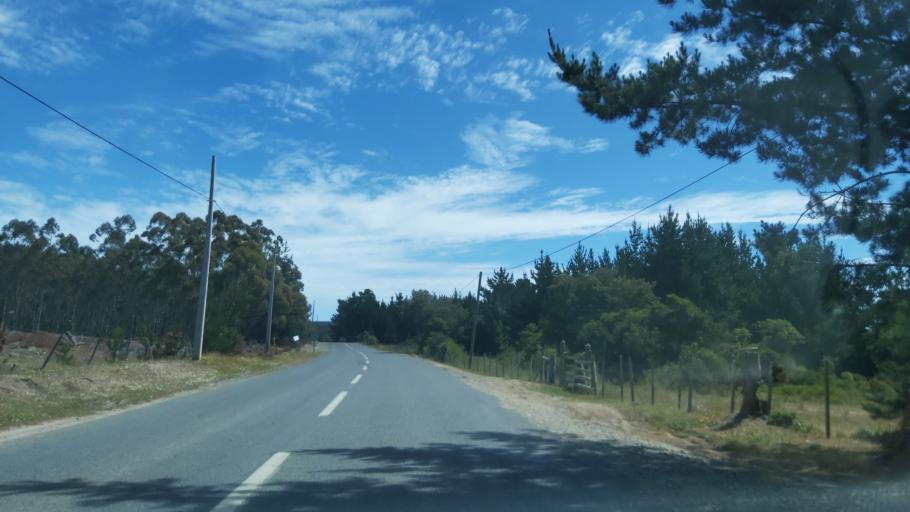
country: CL
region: Maule
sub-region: Provincia de Talca
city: Constitucion
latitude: -35.5425
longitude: -72.5591
